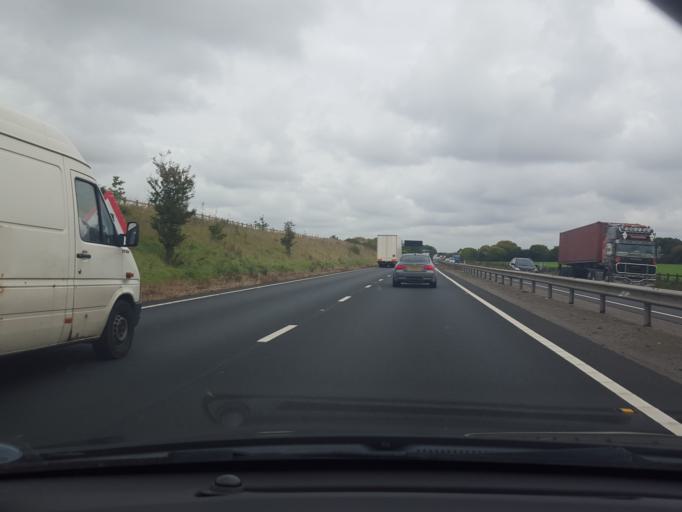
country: GB
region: England
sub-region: Suffolk
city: Capel Saint Mary
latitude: 52.0197
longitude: 1.0786
